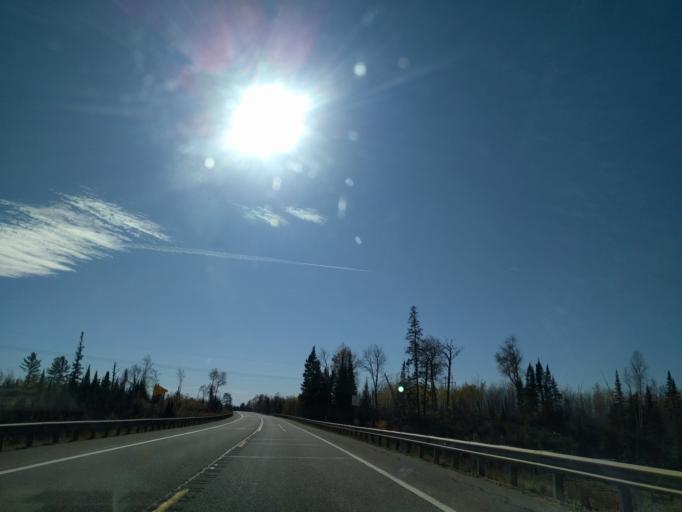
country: US
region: Michigan
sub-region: Marquette County
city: West Ishpeming
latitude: 46.4361
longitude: -87.9643
